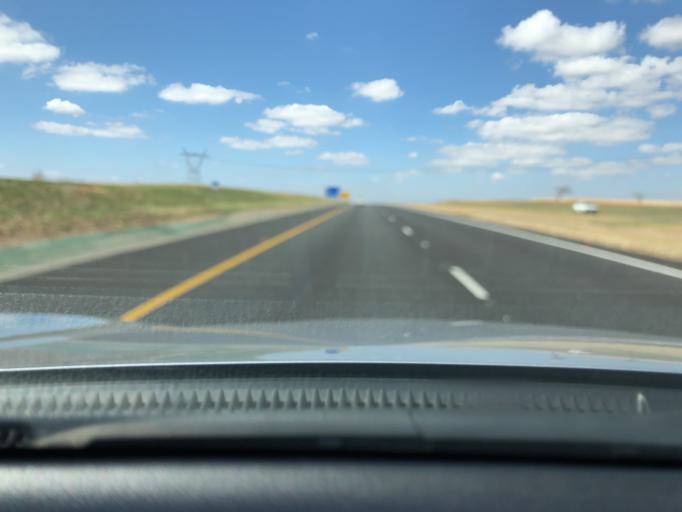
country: ZA
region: KwaZulu-Natal
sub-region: uThukela District Municipality
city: Estcourt
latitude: -28.8650
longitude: 29.7321
